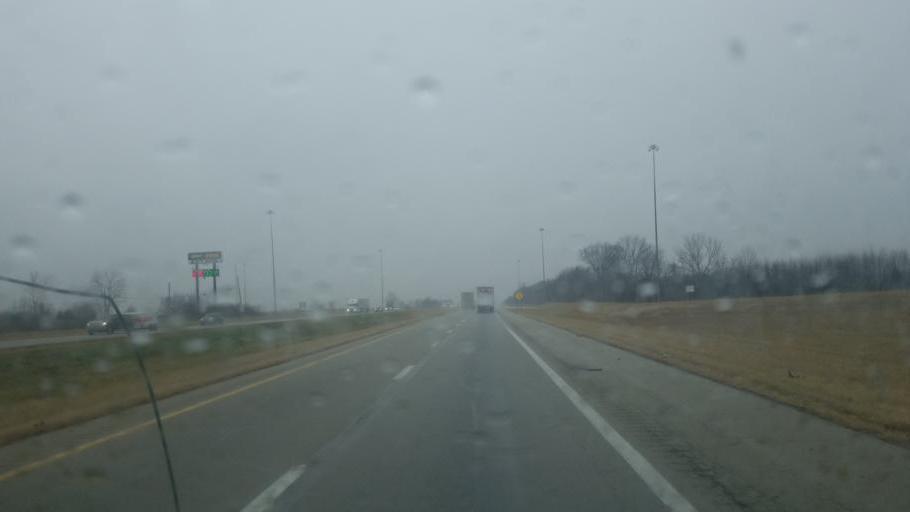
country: US
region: Ohio
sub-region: Preble County
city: Lewisburg
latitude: 39.8356
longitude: -84.6305
